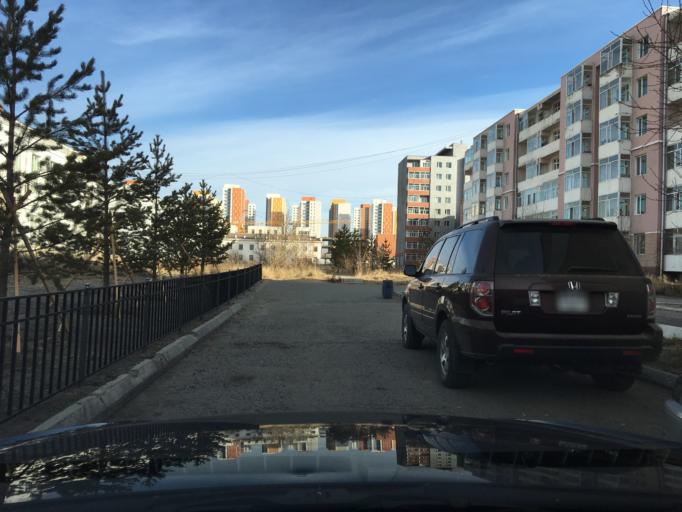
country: MN
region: Ulaanbaatar
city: Ulaanbaatar
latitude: 47.8954
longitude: 106.9142
